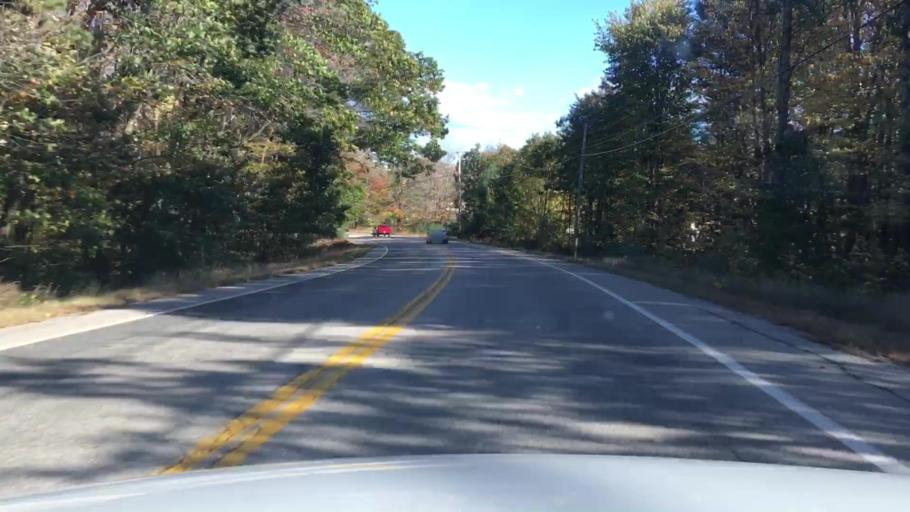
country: US
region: Maine
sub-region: York County
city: South Sanford
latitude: 43.4020
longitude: -70.7267
